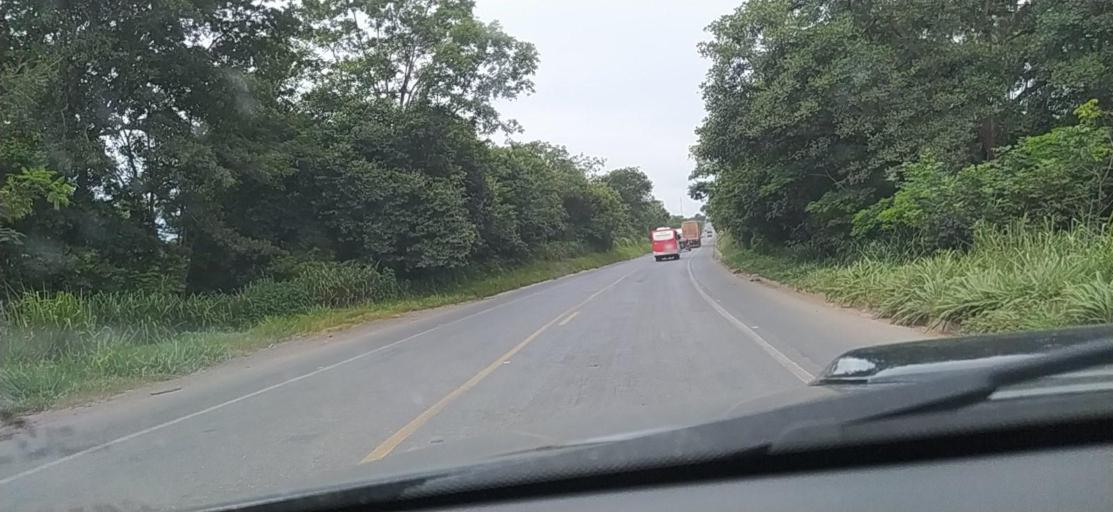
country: BR
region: Minas Gerais
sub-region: Montes Claros
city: Montes Claros
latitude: -16.6641
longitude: -43.7820
